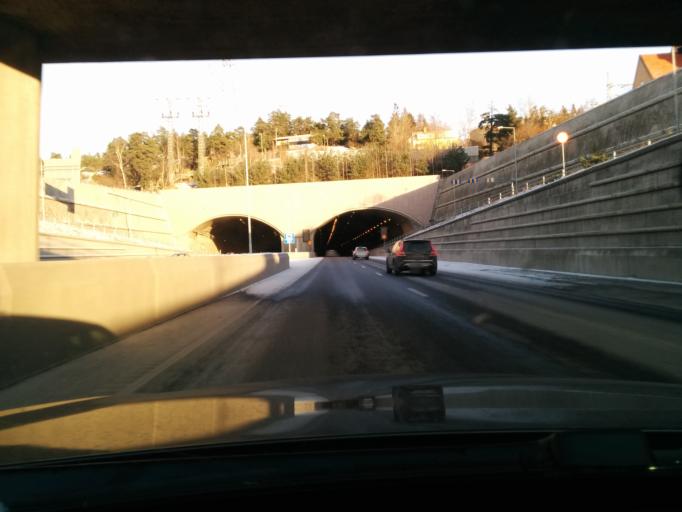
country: SE
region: Stockholm
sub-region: Sollentuna Kommun
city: Sollentuna
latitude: 59.4470
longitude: 17.9425
